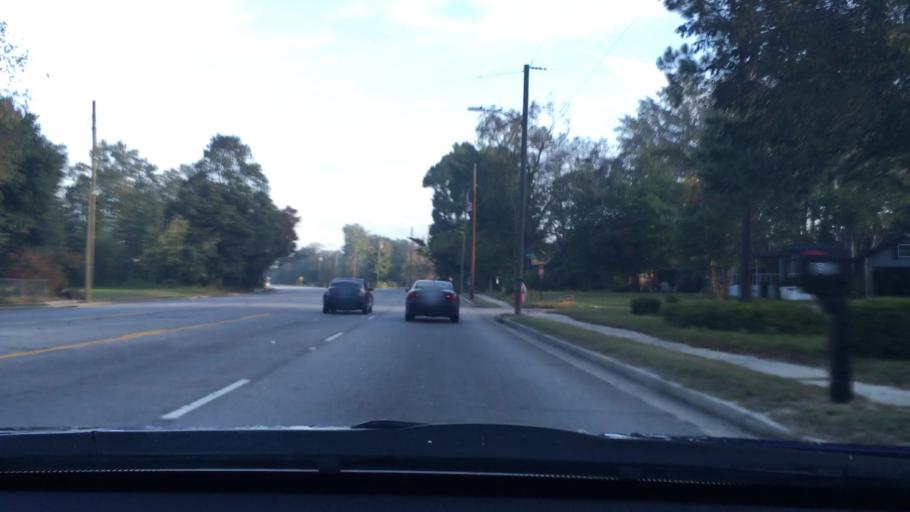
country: US
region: South Carolina
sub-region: Sumter County
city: South Sumter
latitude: 33.9034
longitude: -80.3370
